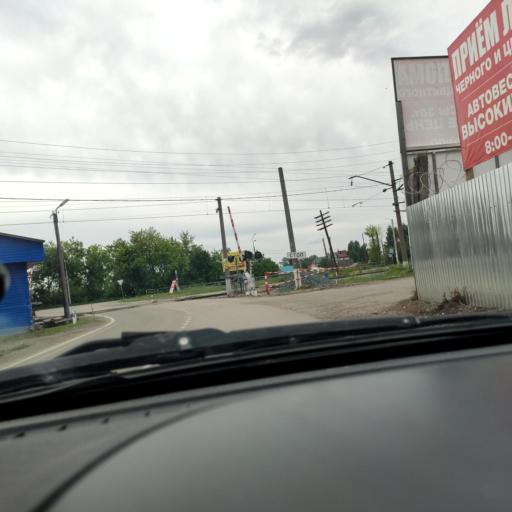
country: RU
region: Perm
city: Overyata
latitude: 58.0619
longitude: 55.8189
